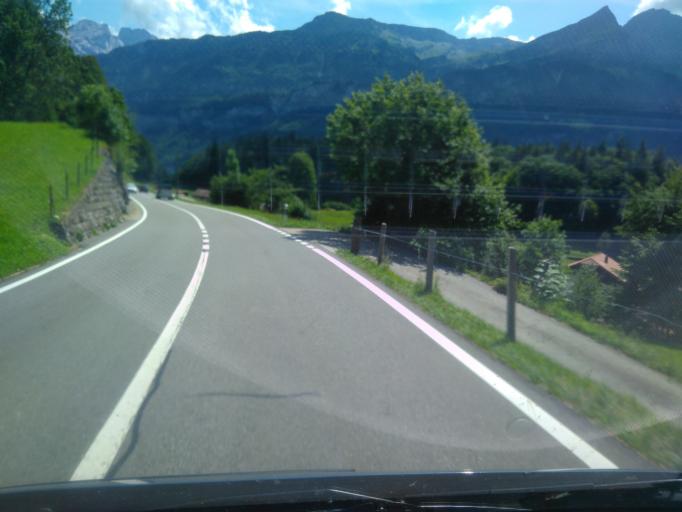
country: CH
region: Obwalden
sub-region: Obwalden
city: Lungern
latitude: 46.7524
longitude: 8.1377
